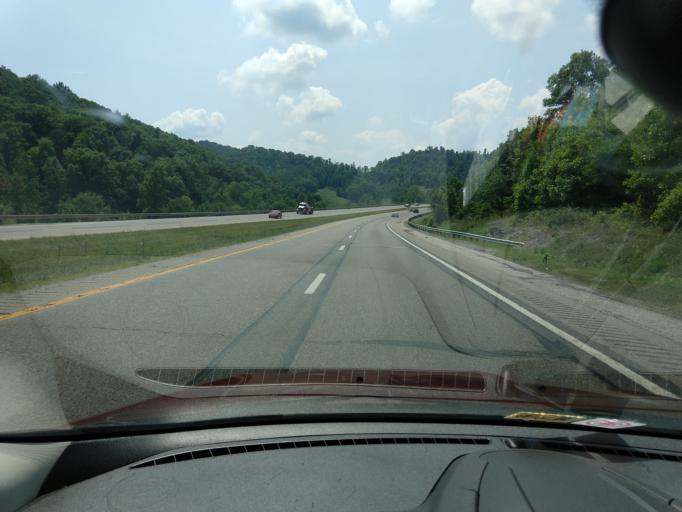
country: US
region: West Virginia
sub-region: Kanawha County
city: Charleston
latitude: 38.4273
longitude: -81.6239
